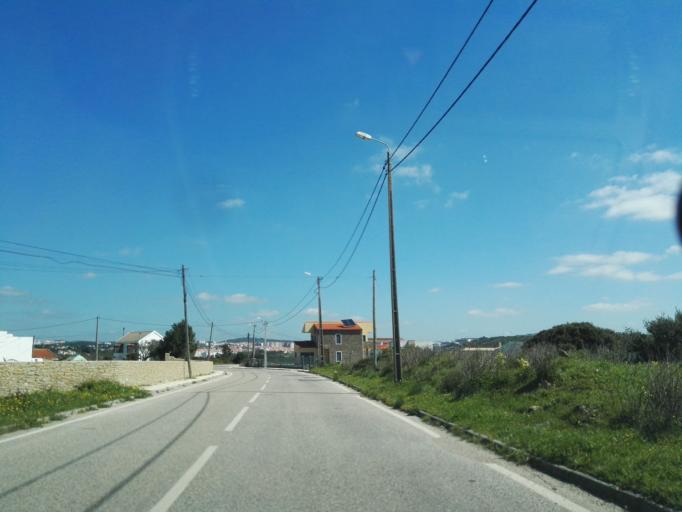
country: PT
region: Lisbon
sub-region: Sintra
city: Rio de Mouro
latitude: 38.7522
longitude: -9.3353
